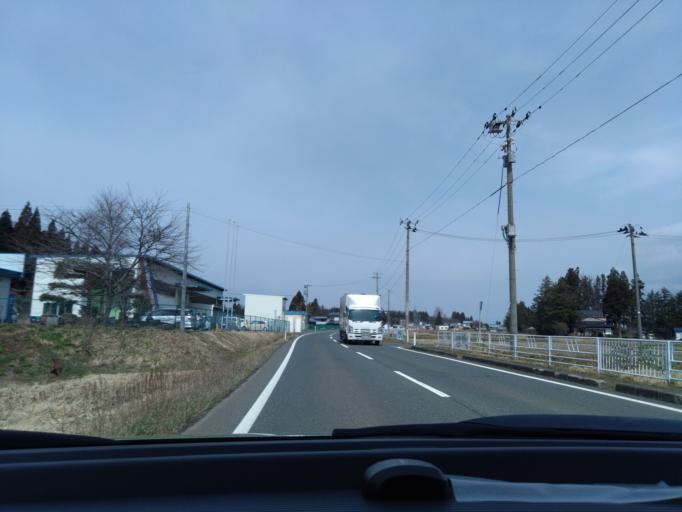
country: JP
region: Iwate
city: Hanamaki
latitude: 39.4947
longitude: 141.1115
